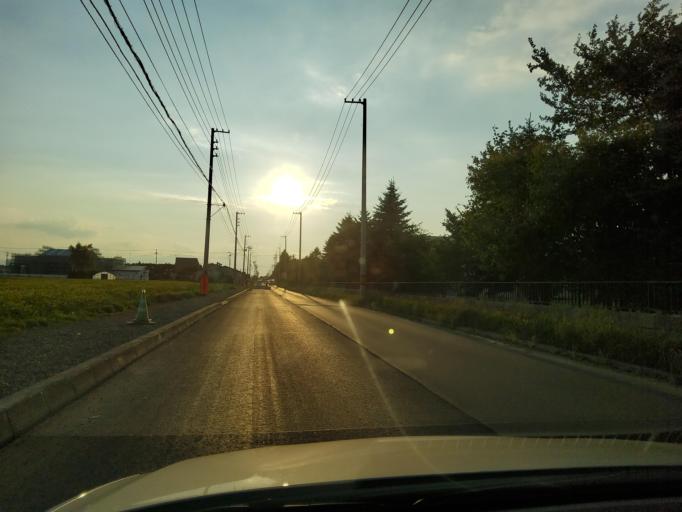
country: JP
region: Hokkaido
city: Obihiro
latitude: 42.9388
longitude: 143.1580
